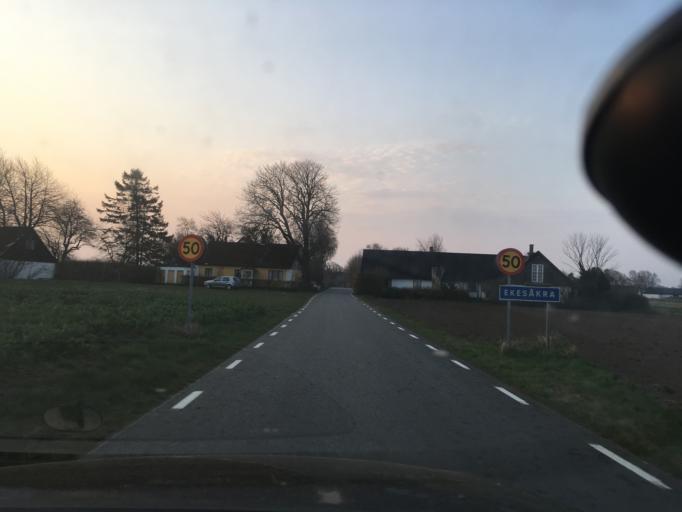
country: SE
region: Skane
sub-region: Ystads Kommun
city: Kopingebro
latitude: 55.4027
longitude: 14.1618
